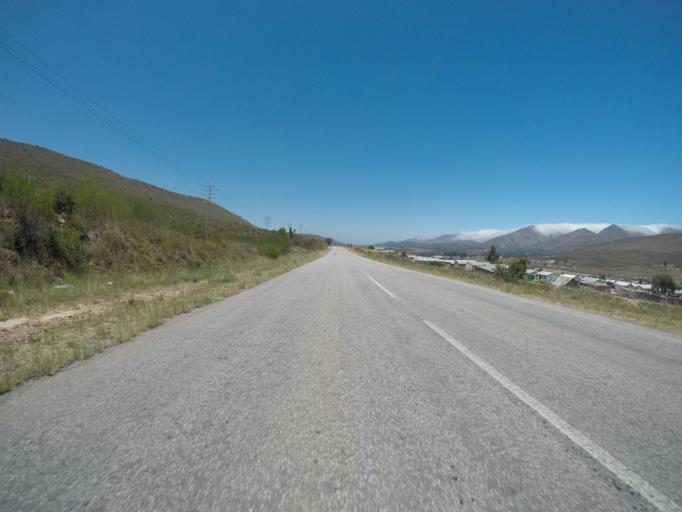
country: ZA
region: Eastern Cape
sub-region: Cacadu District Municipality
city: Kareedouw
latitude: -33.8270
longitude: 23.8759
